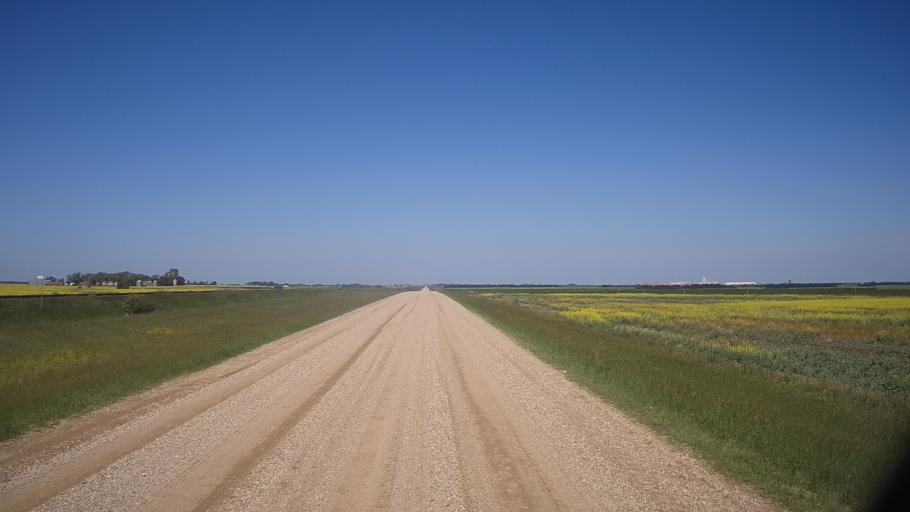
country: CA
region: Saskatchewan
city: Watrous
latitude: 51.8659
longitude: -105.9792
